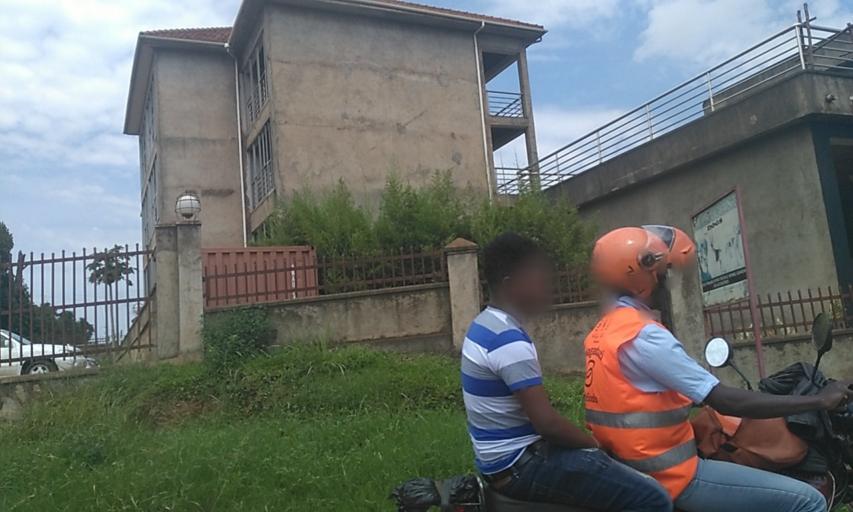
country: UG
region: Central Region
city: Kampala Central Division
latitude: 0.3070
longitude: 32.5522
